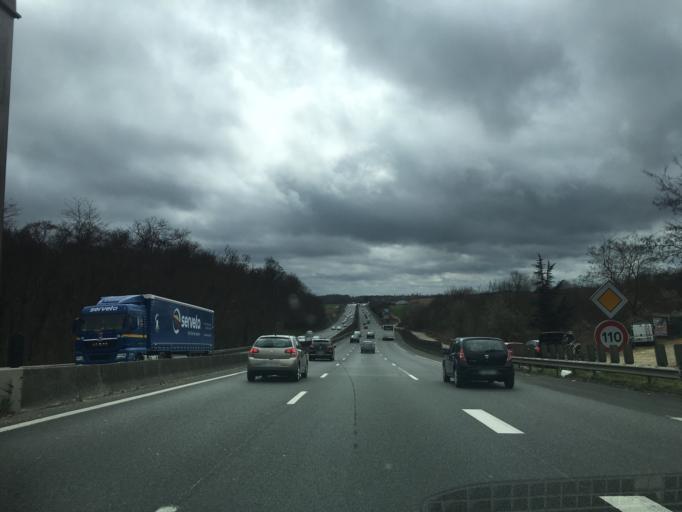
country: FR
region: Ile-de-France
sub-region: Departement de Seine-et-Marne
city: Brie-Comte-Robert
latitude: 48.6737
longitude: 2.6109
